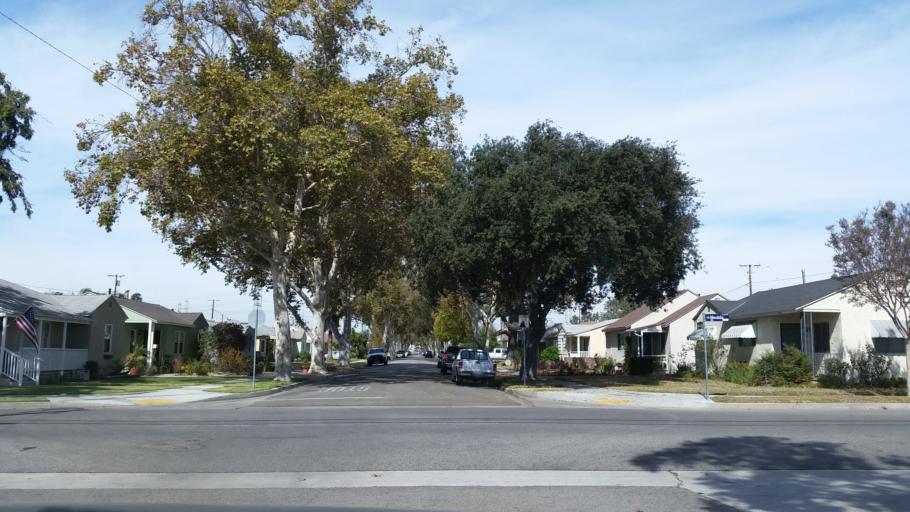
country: US
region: California
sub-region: Los Angeles County
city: Lakewood
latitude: 33.8639
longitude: -118.1401
